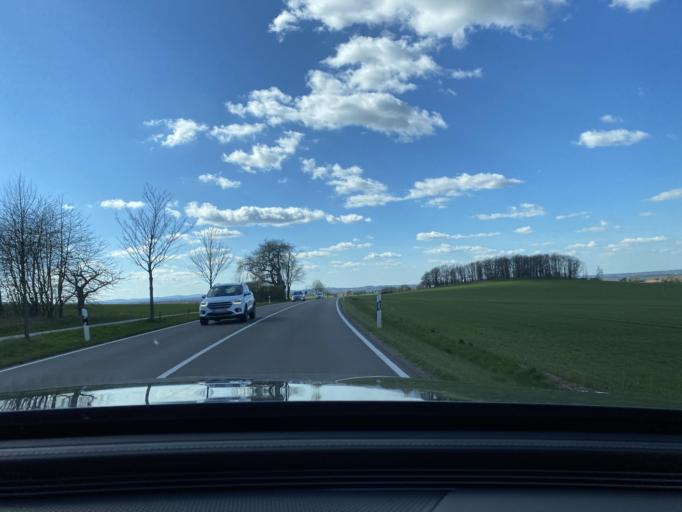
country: DE
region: Saxony
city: Hochkirch
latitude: 51.1542
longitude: 14.5409
